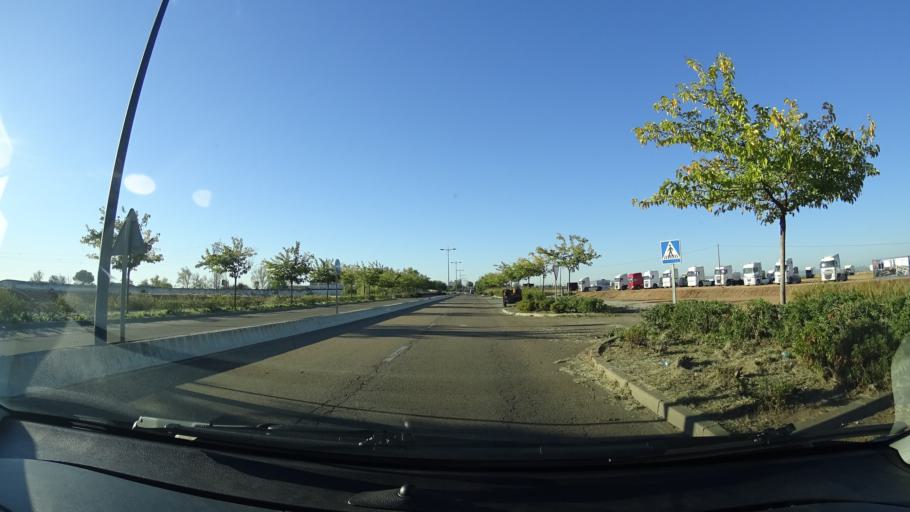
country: ES
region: Extremadura
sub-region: Provincia de Badajoz
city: Almendralejo
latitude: 38.7083
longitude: -6.4002
